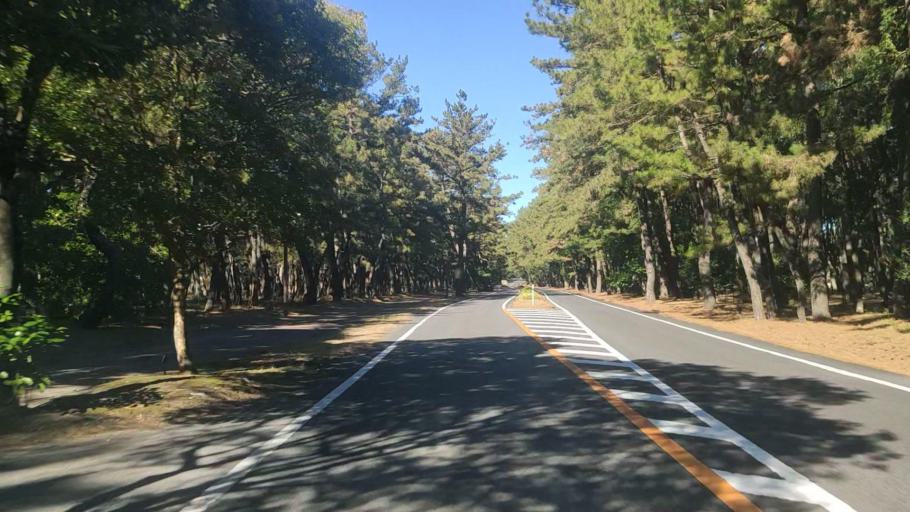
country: JP
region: Miyazaki
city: Miyazaki-shi
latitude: 31.9407
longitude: 131.4649
